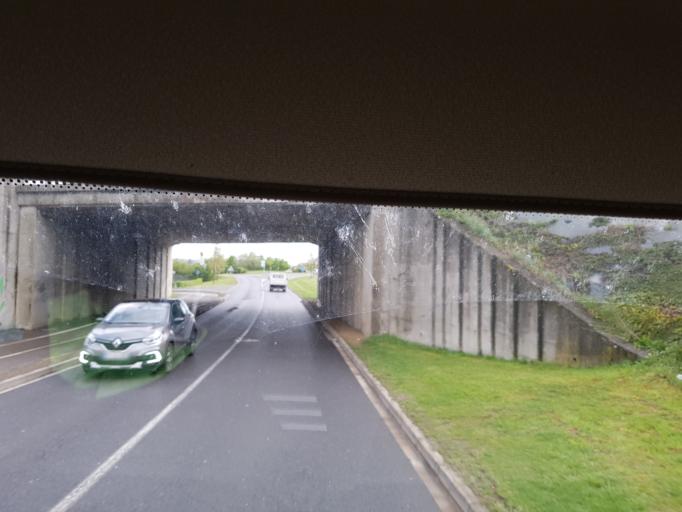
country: FR
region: Picardie
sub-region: Departement de l'Aisne
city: Courmelles
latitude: 49.3607
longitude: 3.3160
